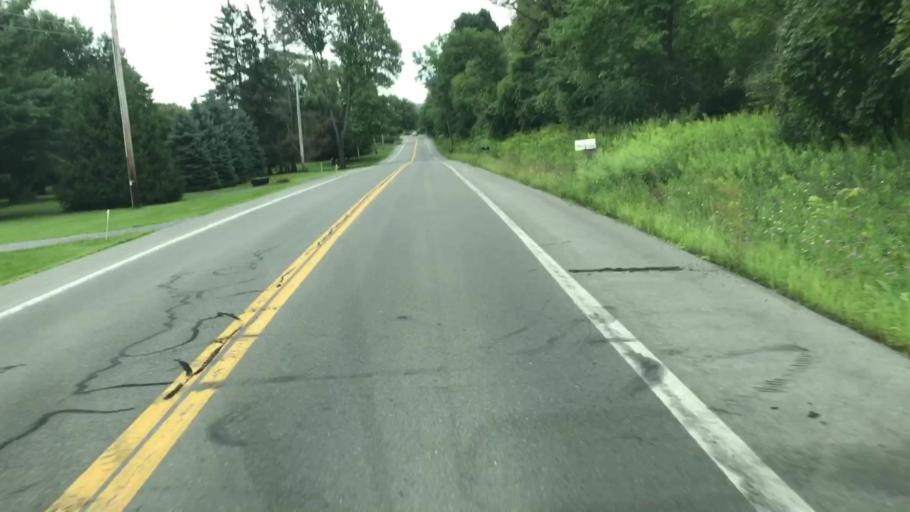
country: US
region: New York
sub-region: Onondaga County
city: Camillus
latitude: 43.0598
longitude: -76.3202
